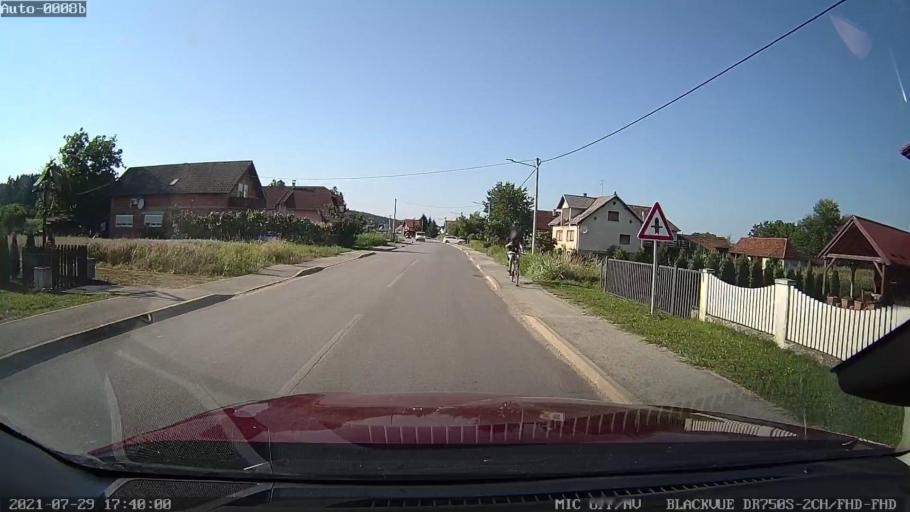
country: HR
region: Varazdinska
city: Vinica
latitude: 46.3192
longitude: 16.1564
